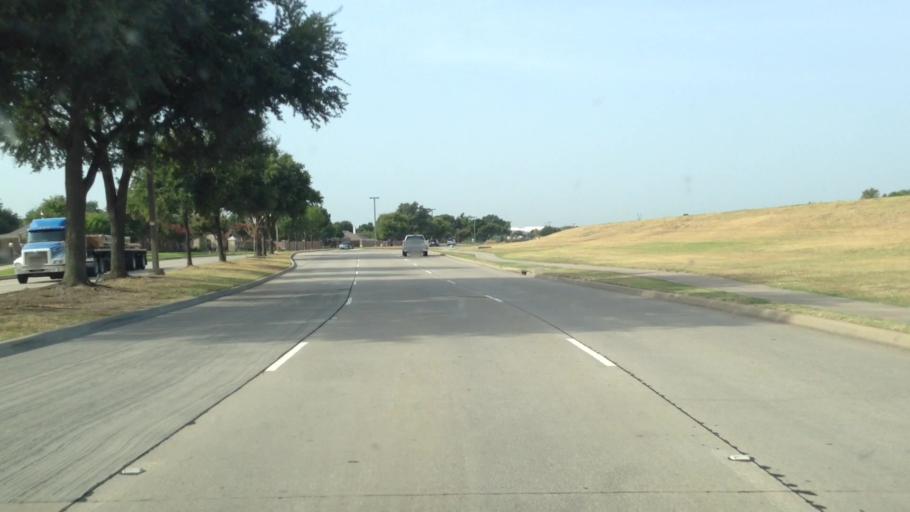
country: US
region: Texas
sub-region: Denton County
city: Lewisville
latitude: 33.0218
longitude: -96.9424
